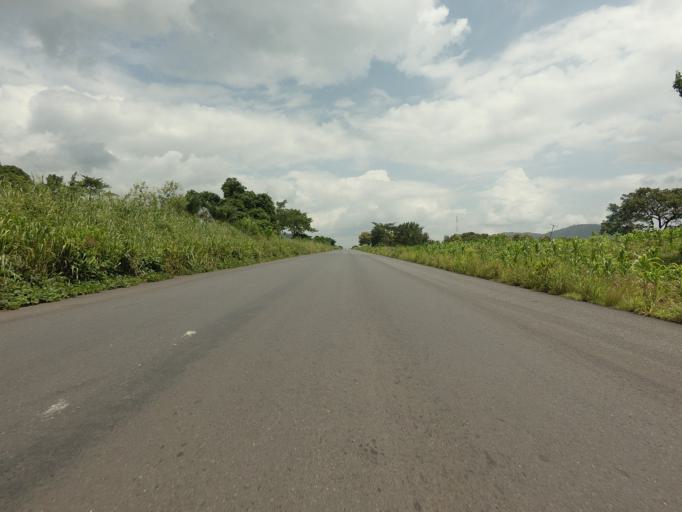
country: GH
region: Volta
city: Ho
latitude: 6.5569
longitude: 0.2607
